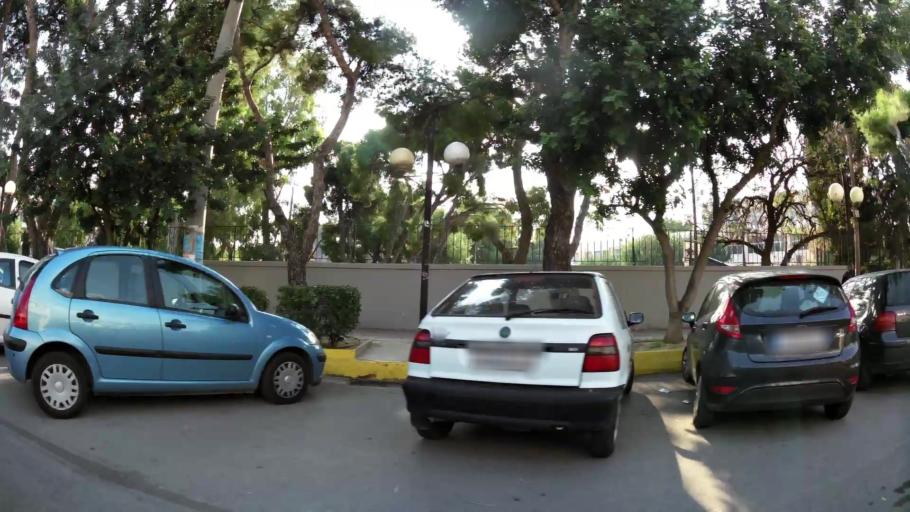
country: GR
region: Attica
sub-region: Nomarchia Athinas
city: Nea Filadelfeia
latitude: 38.0372
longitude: 23.7378
